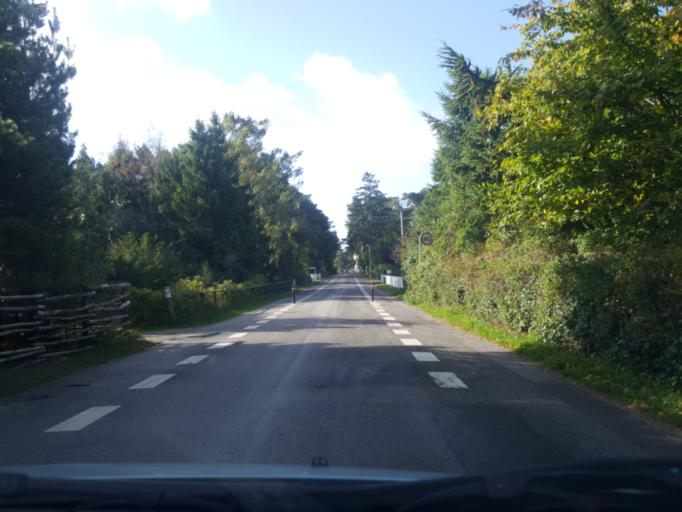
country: DK
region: Zealand
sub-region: Guldborgsund Kommune
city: Nykobing Falster
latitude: 54.6796
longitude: 11.9614
